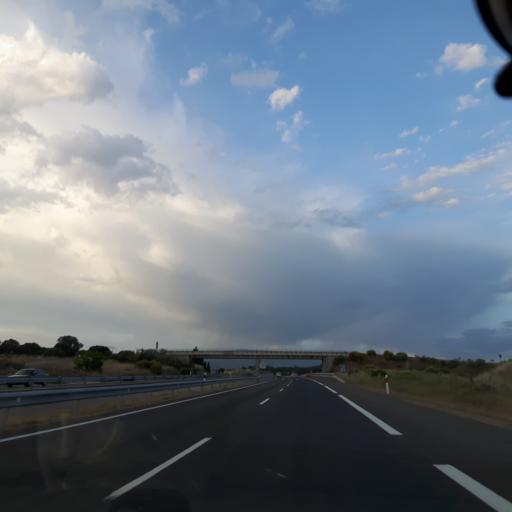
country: ES
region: Castille and Leon
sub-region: Provincia de Salamanca
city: Fuentes de Bejar
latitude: 40.5060
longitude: -5.6756
